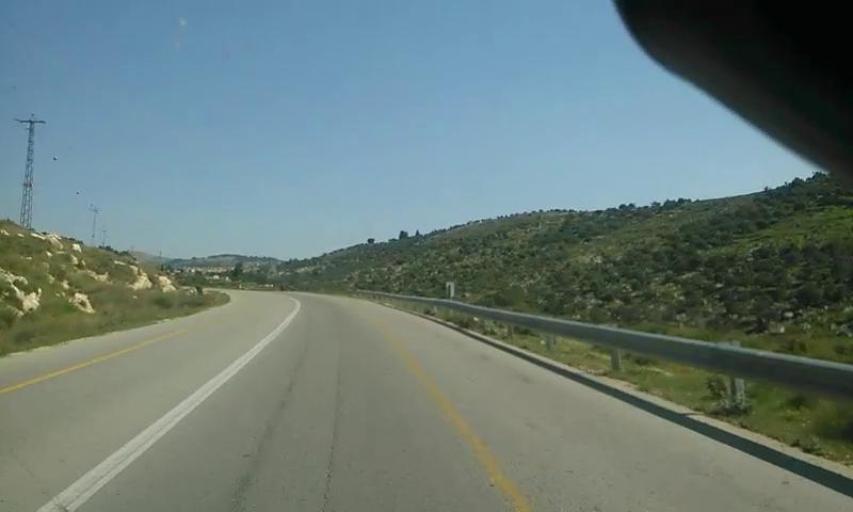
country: PS
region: West Bank
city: Tarqumya
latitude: 31.5641
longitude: 34.9968
